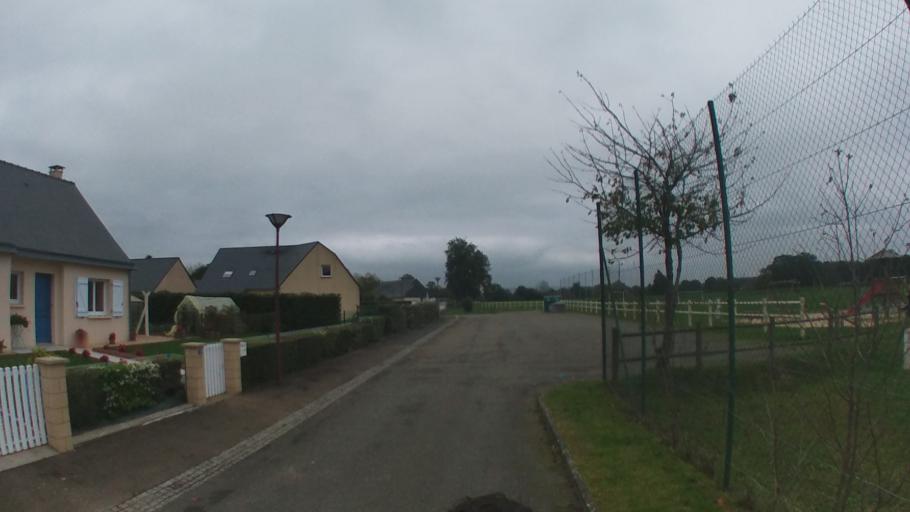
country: FR
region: Pays de la Loire
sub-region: Departement de la Mayenne
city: Aron
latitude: 48.3461
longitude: -0.5743
